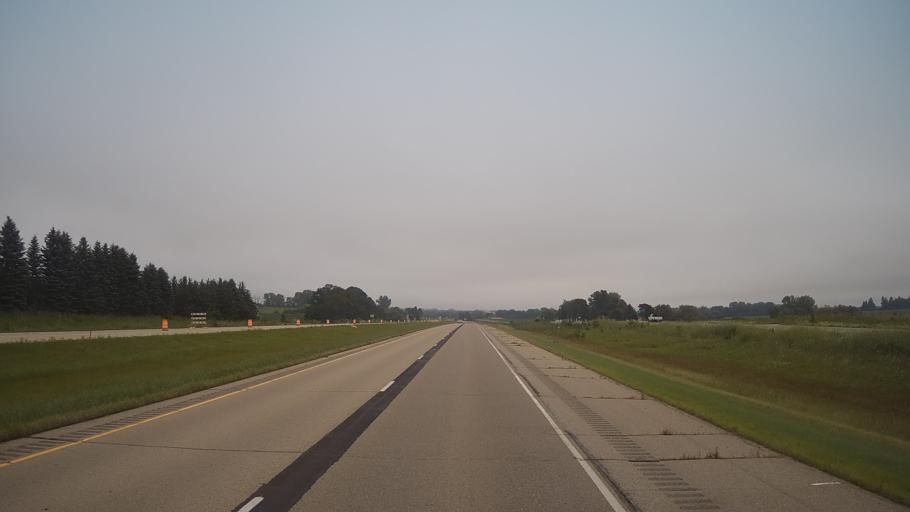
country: US
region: Minnesota
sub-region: Olmsted County
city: Stewartville
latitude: 43.8316
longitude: -92.5560
